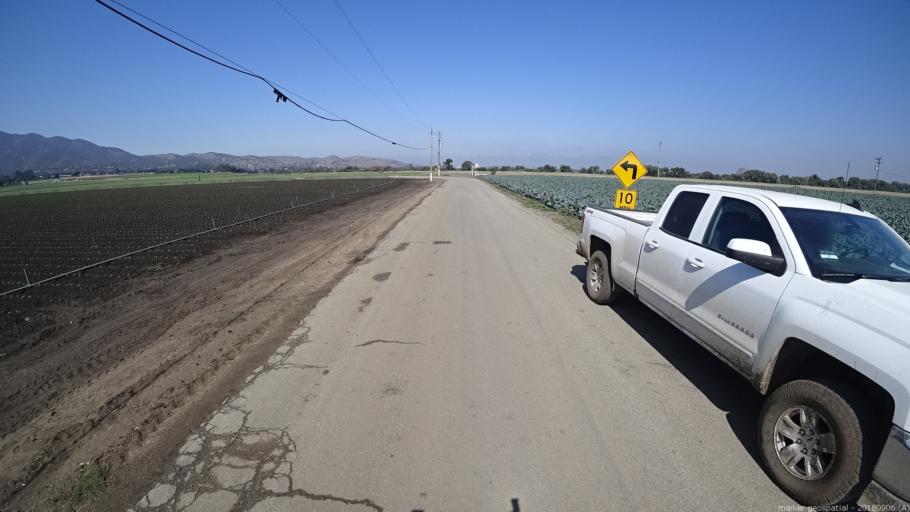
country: US
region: California
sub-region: Monterey County
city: Salinas
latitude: 36.6012
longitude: -121.6147
